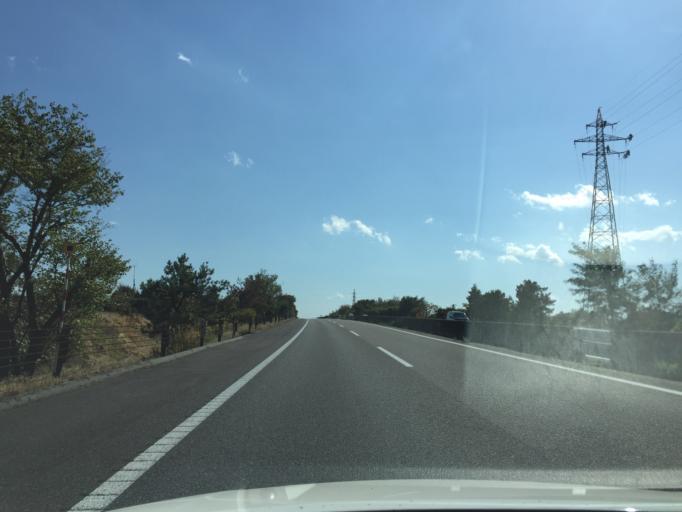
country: JP
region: Fukushima
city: Sukagawa
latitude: 37.3083
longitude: 140.3458
